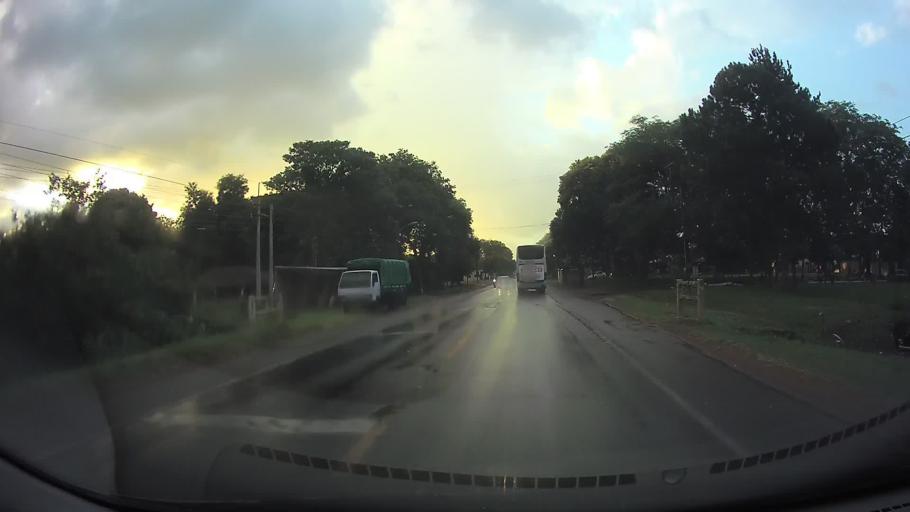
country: PY
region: Paraguari
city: Paraguari
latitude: -25.6023
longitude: -57.1916
